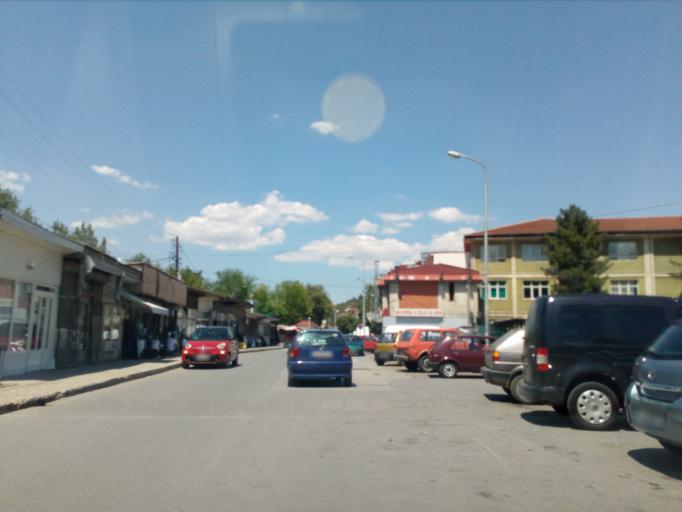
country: MK
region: Veles
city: Veles
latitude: 41.7129
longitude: 21.7856
